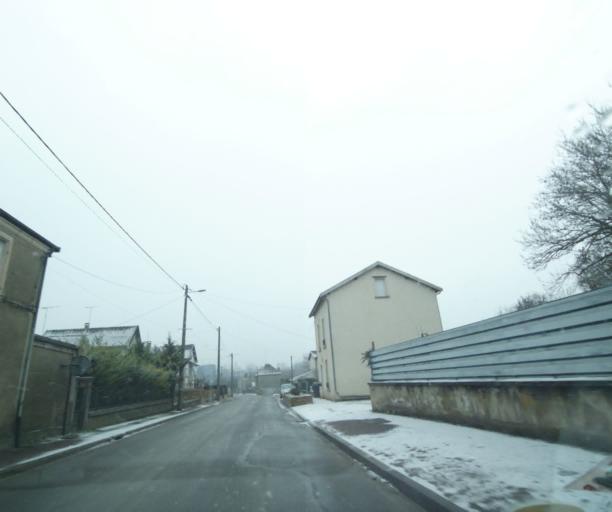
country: FR
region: Champagne-Ardenne
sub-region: Departement de la Haute-Marne
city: Wassy
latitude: 48.4948
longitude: 4.9538
